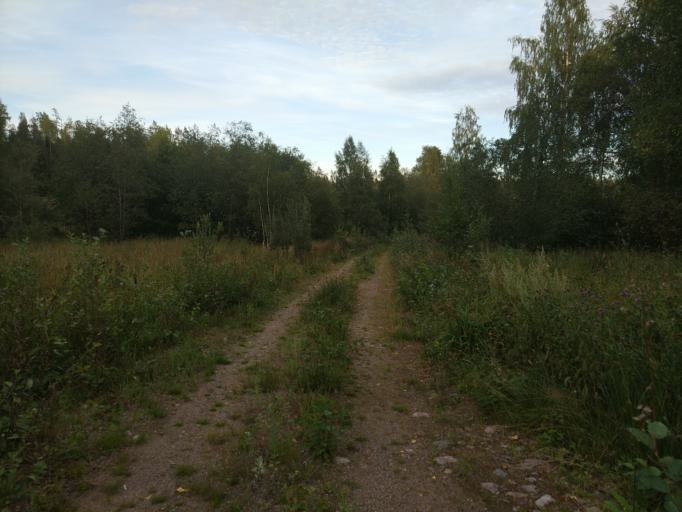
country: RU
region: Leningrad
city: Kuznechnoye
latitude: 61.1146
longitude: 29.6076
